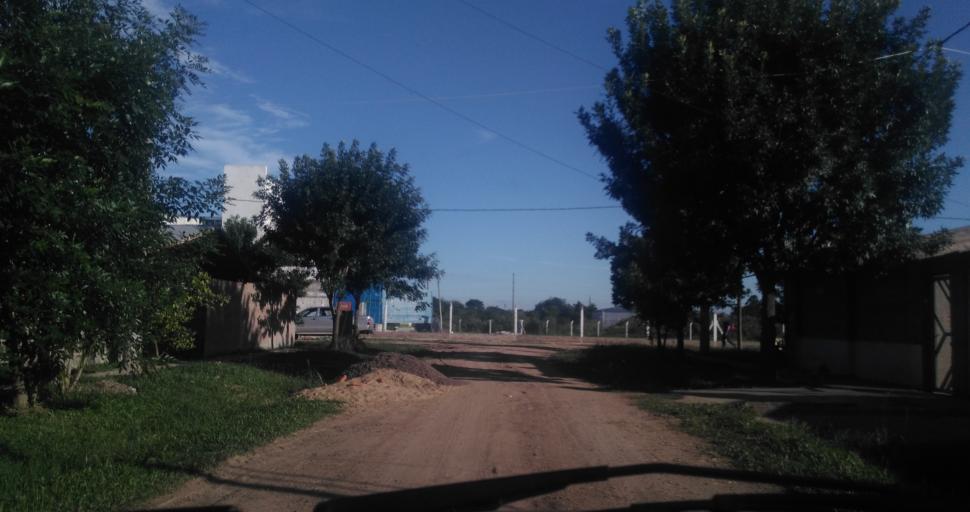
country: AR
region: Chaco
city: Fontana
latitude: -27.4149
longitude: -59.0245
